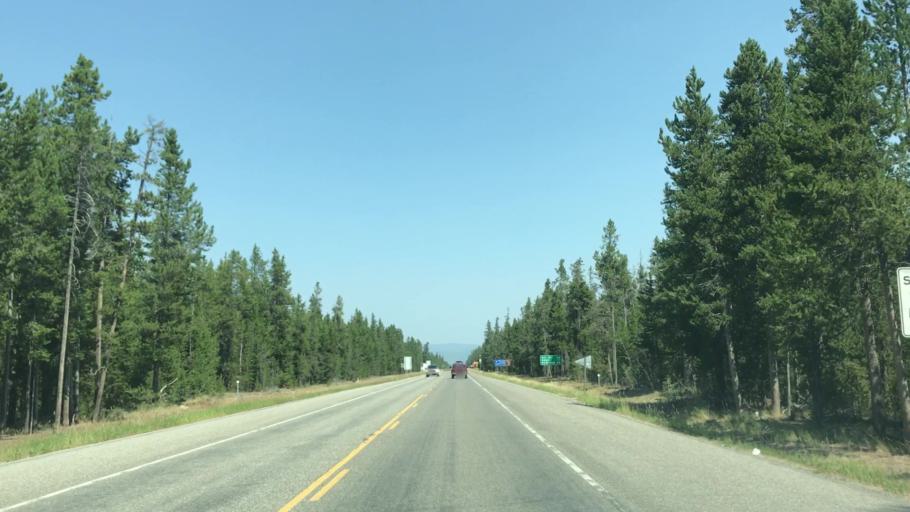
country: US
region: Montana
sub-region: Gallatin County
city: West Yellowstone
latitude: 44.6691
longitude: -111.1001
